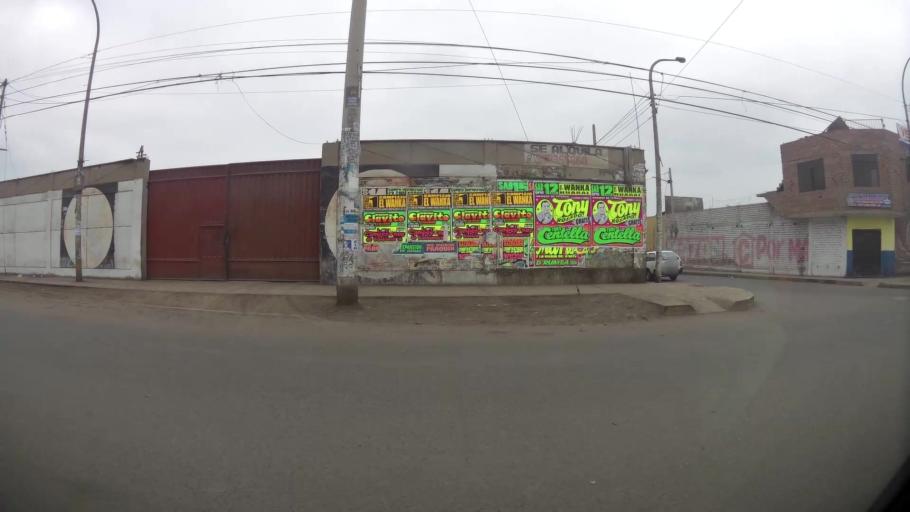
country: PE
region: Lima
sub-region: Provincia de Huaral
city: Huaral
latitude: -11.4948
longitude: -77.2015
